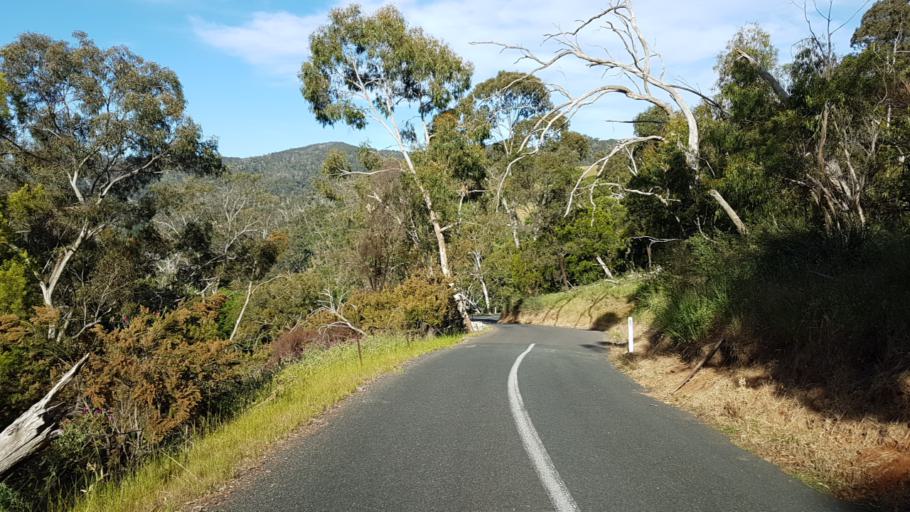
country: AU
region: South Australia
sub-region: Adelaide Hills
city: Adelaide Hills
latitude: -34.9101
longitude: 138.7698
